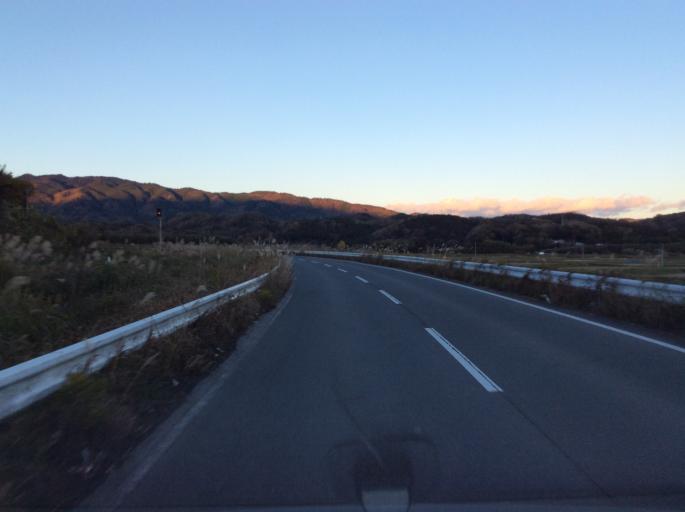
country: JP
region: Fukushima
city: Iwaki
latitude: 37.1200
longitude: 140.8629
